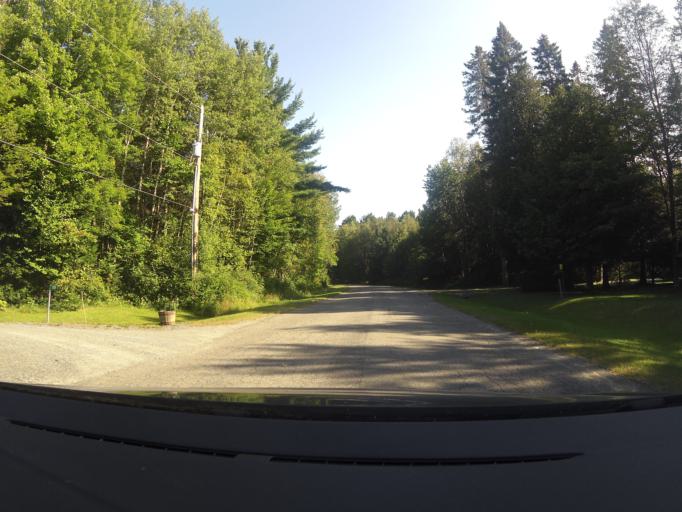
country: CA
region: Ontario
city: Carleton Place
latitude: 45.2984
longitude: -76.0622
